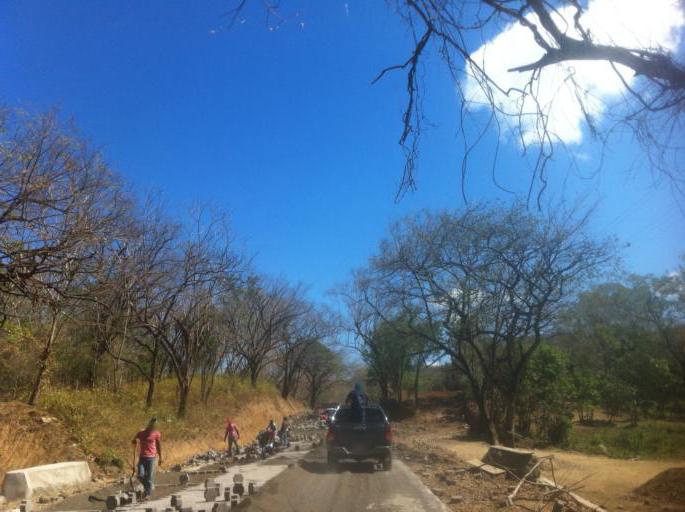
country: NI
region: Rivas
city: Tola
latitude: 11.3985
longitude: -85.9933
